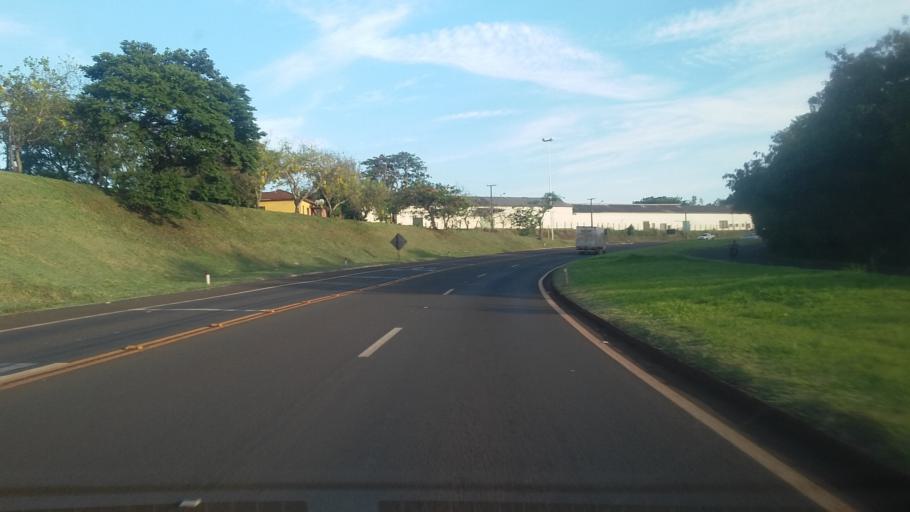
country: BR
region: Parana
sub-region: Assai
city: Assai
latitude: -23.1983
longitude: -50.6543
